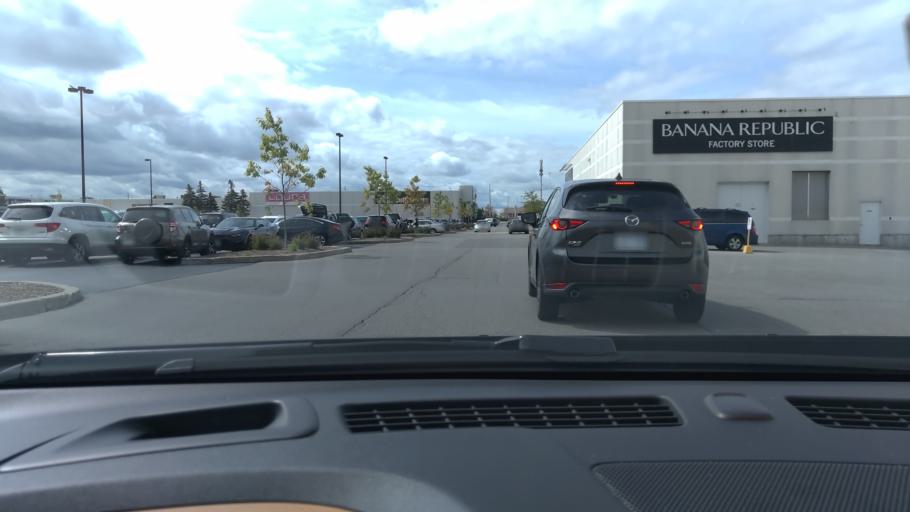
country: CA
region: Ontario
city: Mississauga
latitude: 43.6132
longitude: -79.6917
